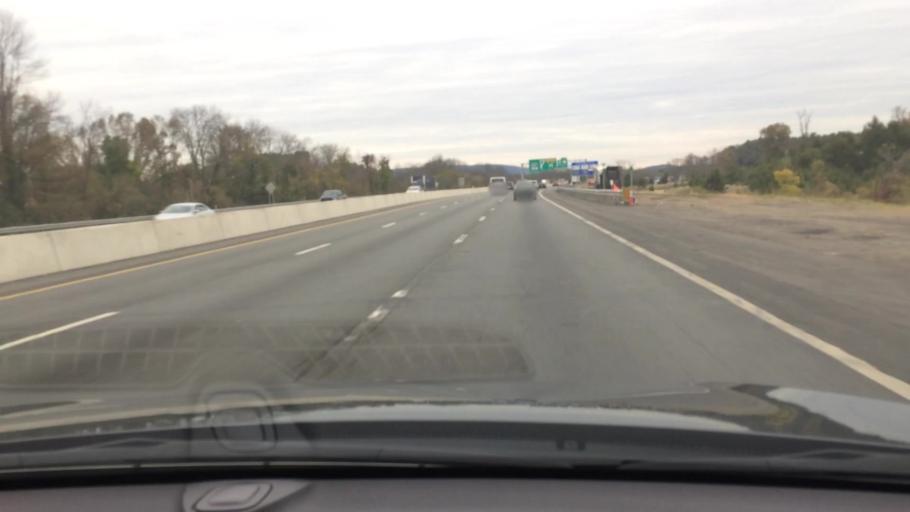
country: US
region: New York
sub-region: Orange County
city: Harriman
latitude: 41.2920
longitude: -74.1392
